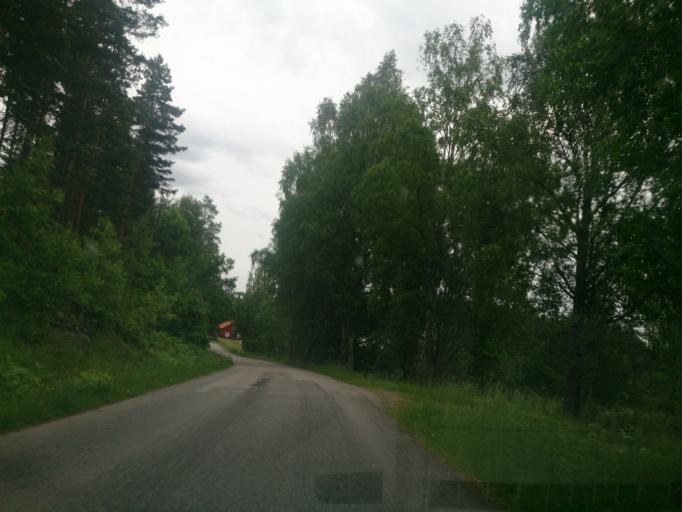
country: SE
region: OEstergoetland
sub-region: Soderkopings Kommun
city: Soederkoeping
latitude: 58.3003
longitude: 16.2564
